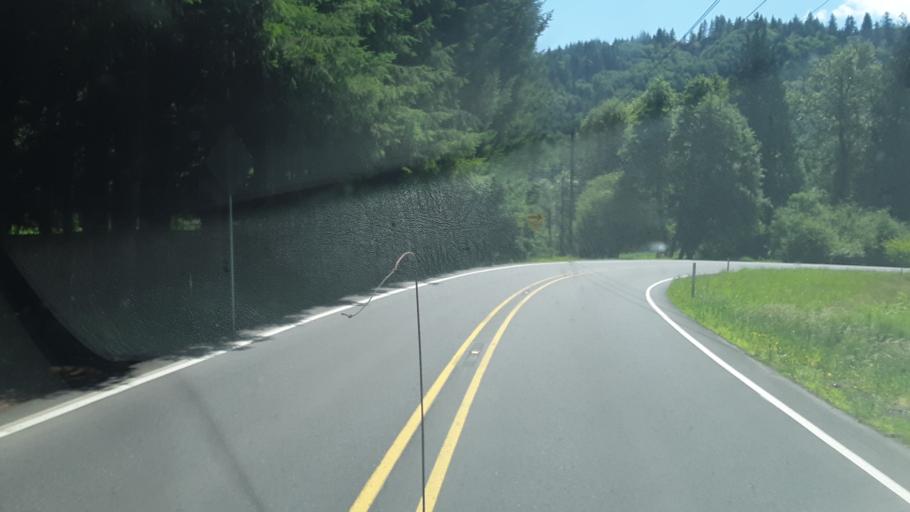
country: US
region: Washington
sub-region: Clark County
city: Yacolt
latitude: 45.9254
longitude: -122.3797
